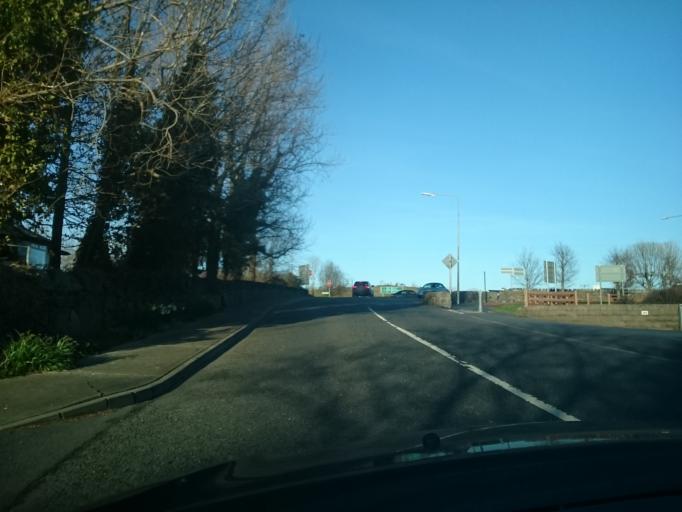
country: IE
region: Connaught
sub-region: Maigh Eo
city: Westport
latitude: 53.8069
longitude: -9.5280
